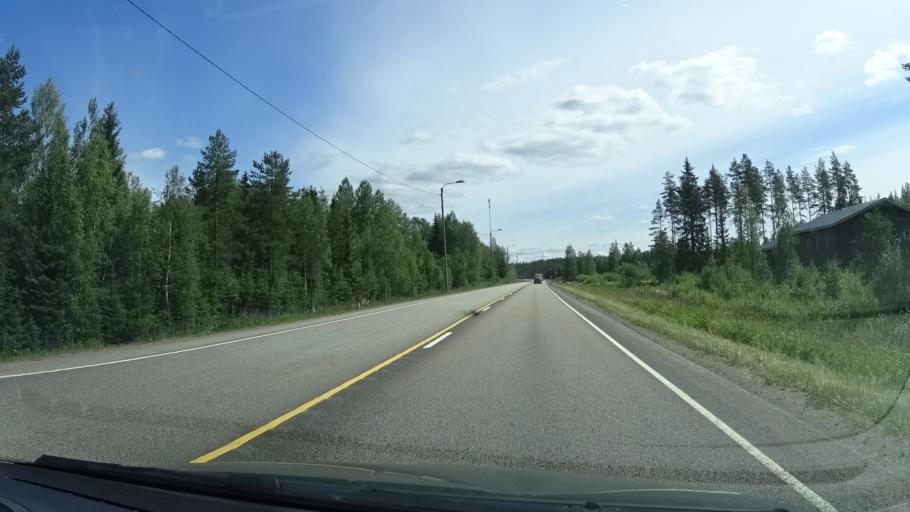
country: FI
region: Central Finland
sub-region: Jyvaeskylae
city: Uurainen
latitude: 62.2652
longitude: 25.4613
